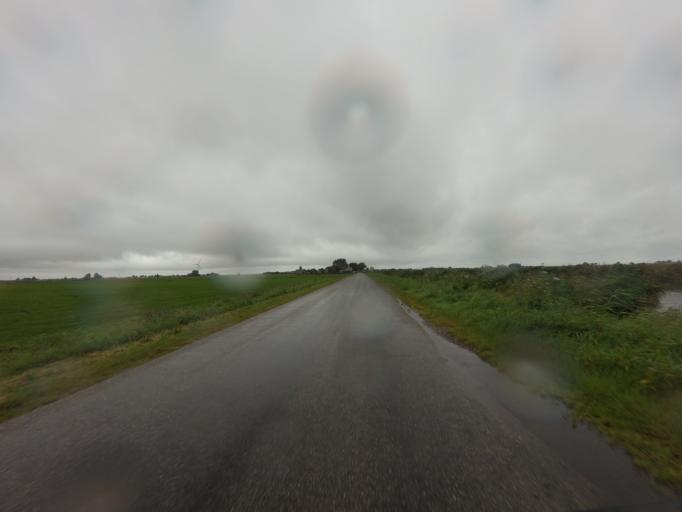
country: NL
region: Friesland
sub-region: Sudwest Fryslan
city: Workum
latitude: 53.0081
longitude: 5.4748
